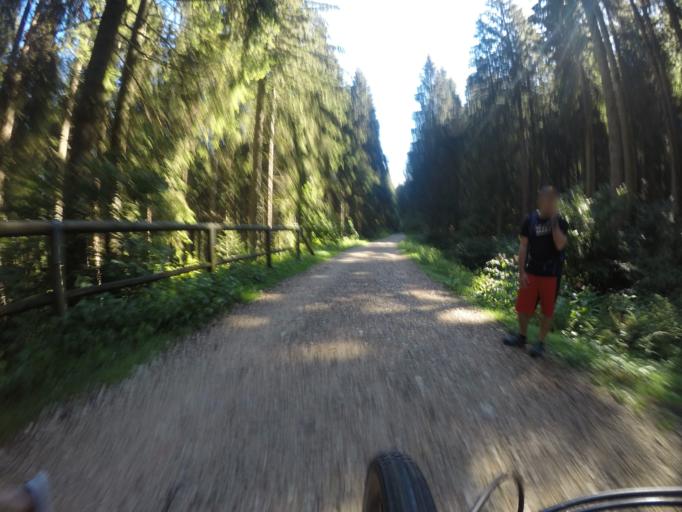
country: IT
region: Veneto
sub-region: Provincia di Vicenza
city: Canove di Roana
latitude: 45.8476
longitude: 11.4712
